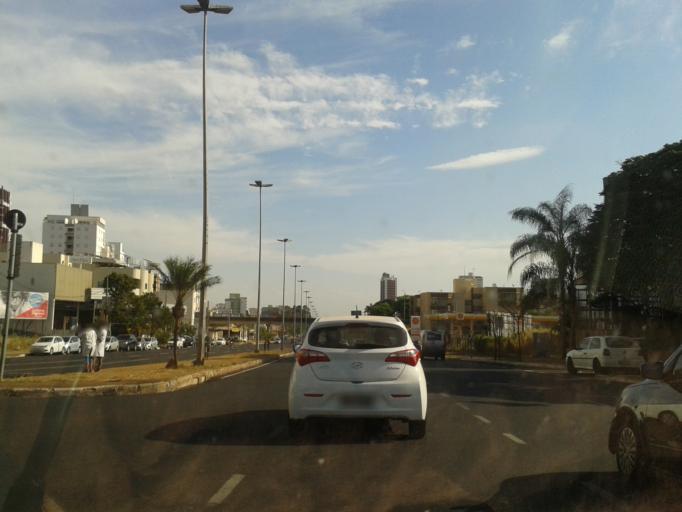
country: BR
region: Minas Gerais
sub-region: Uberlandia
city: Uberlandia
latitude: -18.9175
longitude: -48.2655
